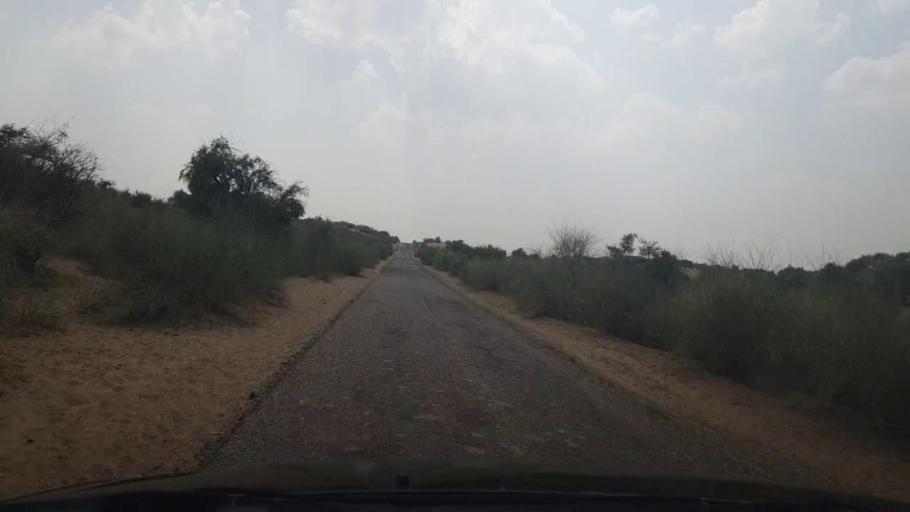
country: PK
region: Sindh
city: Islamkot
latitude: 25.0031
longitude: 70.5010
